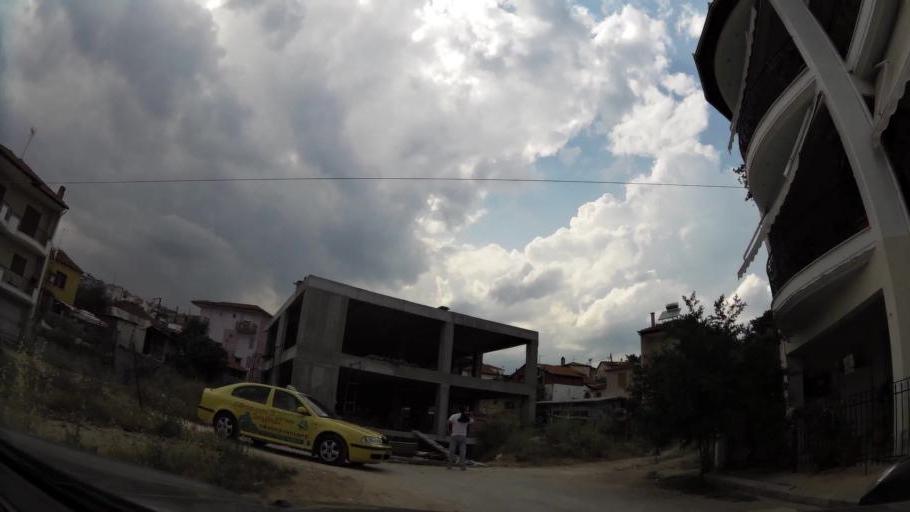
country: GR
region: Central Macedonia
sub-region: Nomos Imathias
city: Veroia
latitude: 40.5193
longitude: 22.2089
